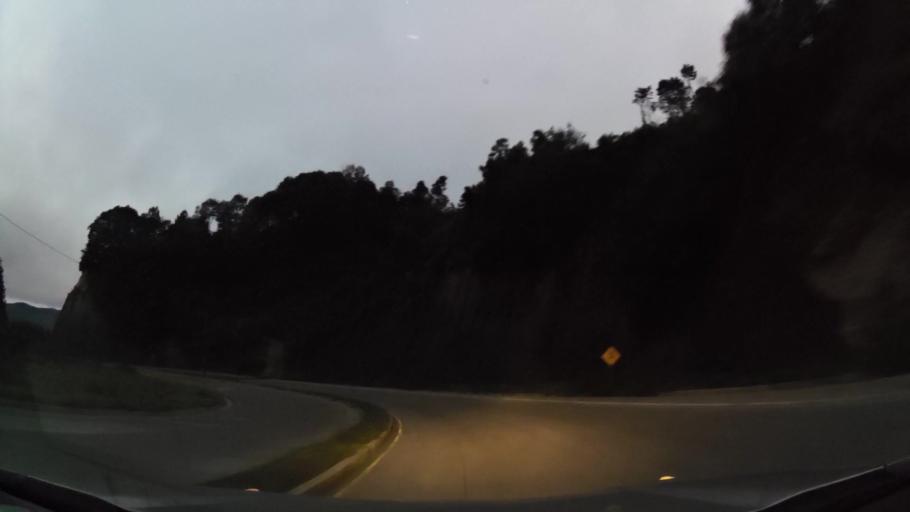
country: GT
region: Chimaltenango
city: Santa Apolonia
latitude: 14.8184
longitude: -91.0036
